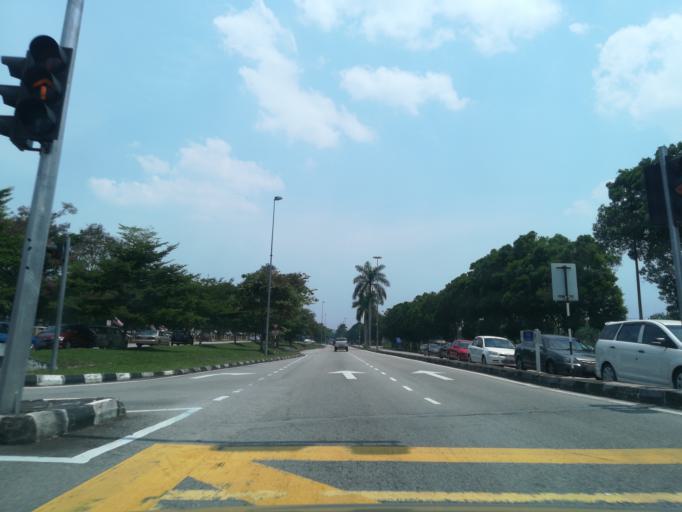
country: MY
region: Kedah
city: Kulim
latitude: 5.3933
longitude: 100.5727
